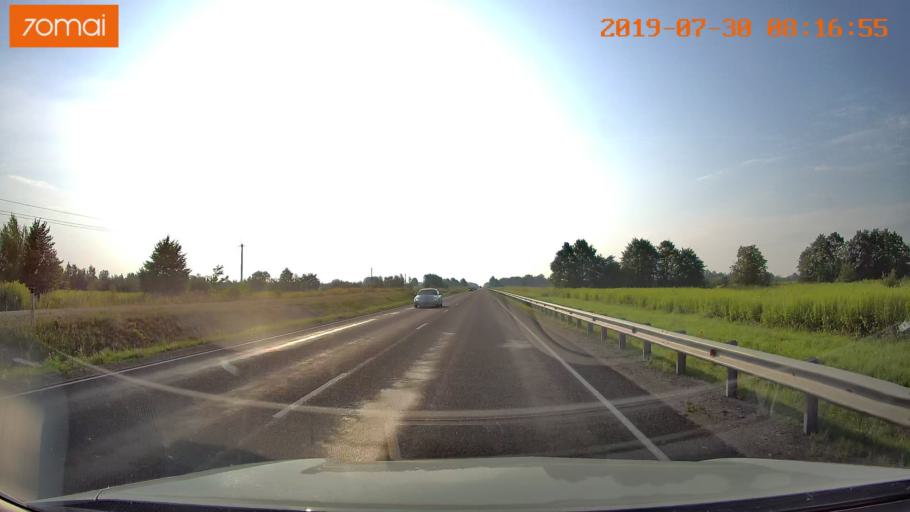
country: RU
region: Kaliningrad
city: Zheleznodorozhnyy
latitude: 54.6384
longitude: 21.4237
